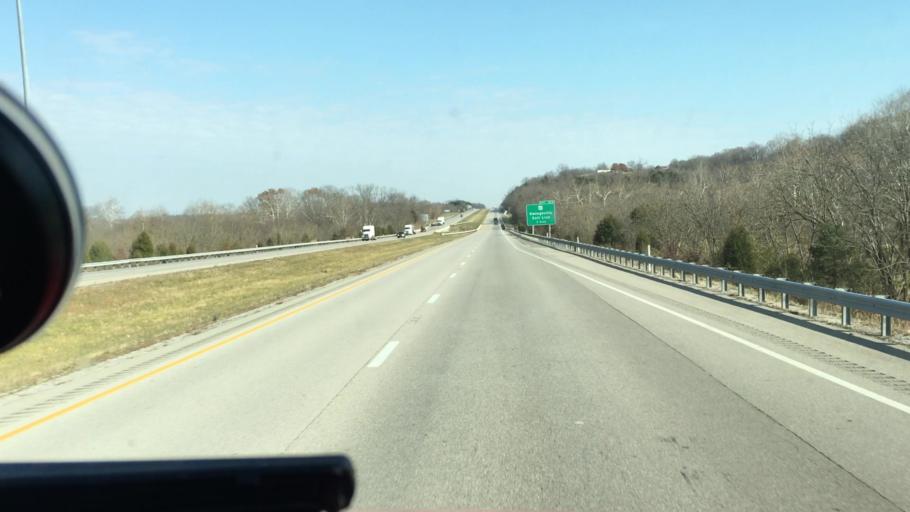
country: US
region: Kentucky
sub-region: Bath County
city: Owingsville
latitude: 38.1294
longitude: -83.7456
